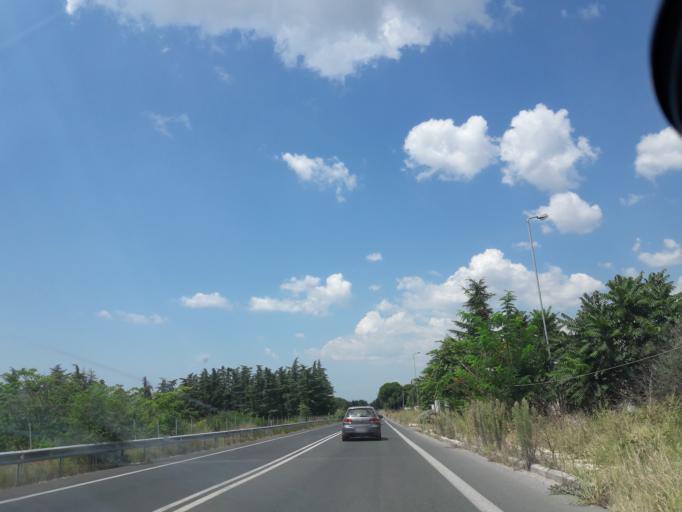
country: GR
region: Central Macedonia
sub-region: Nomos Thessalonikis
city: Souroti
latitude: 40.5078
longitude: 23.0871
